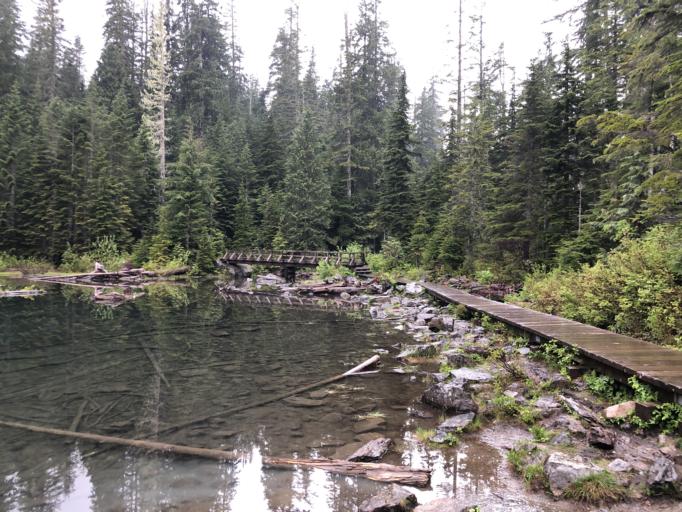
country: US
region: Washington
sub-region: Snohomish County
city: Granite Falls
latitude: 48.0663
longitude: -121.7621
